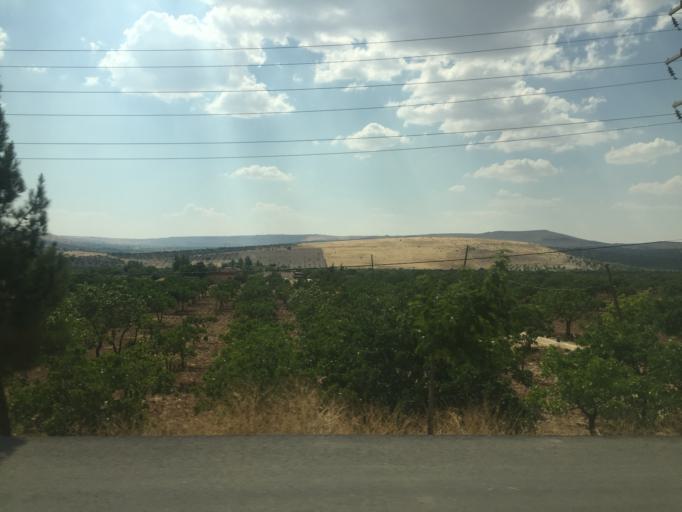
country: TR
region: Sanliurfa
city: Sanliurfa
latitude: 37.2406
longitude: 38.7939
